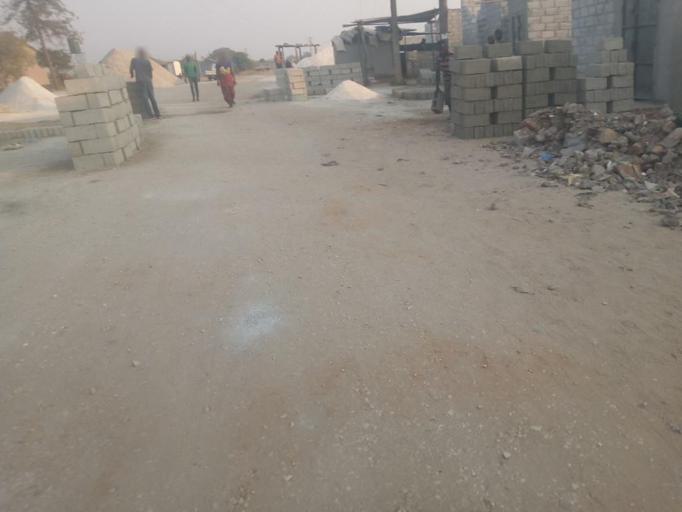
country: ZM
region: Lusaka
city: Lusaka
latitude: -15.4071
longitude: 28.3697
